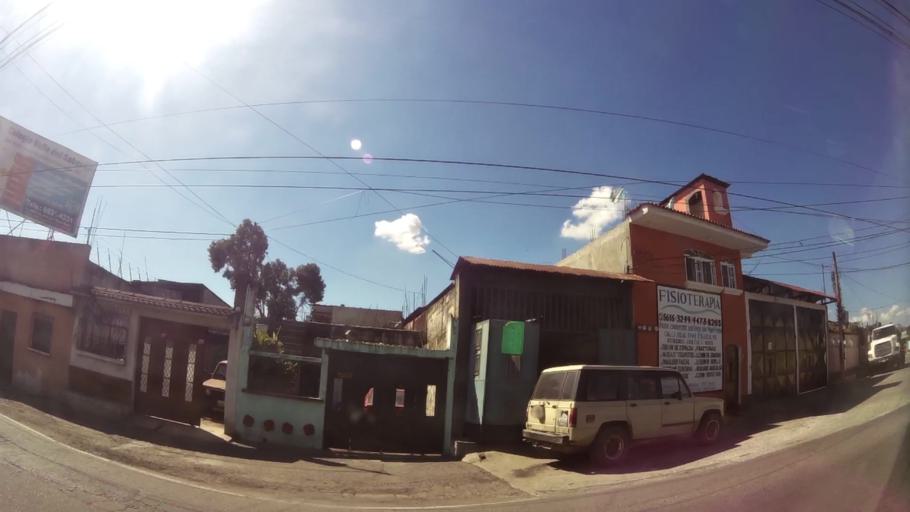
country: GT
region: Guatemala
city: Petapa
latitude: 14.4966
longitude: -90.5570
